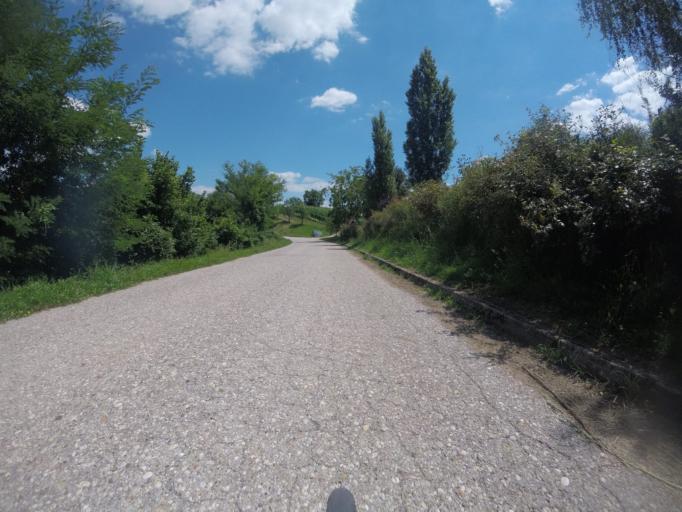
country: HR
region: Karlovacka
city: Ozalj
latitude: 45.6769
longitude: 15.4545
